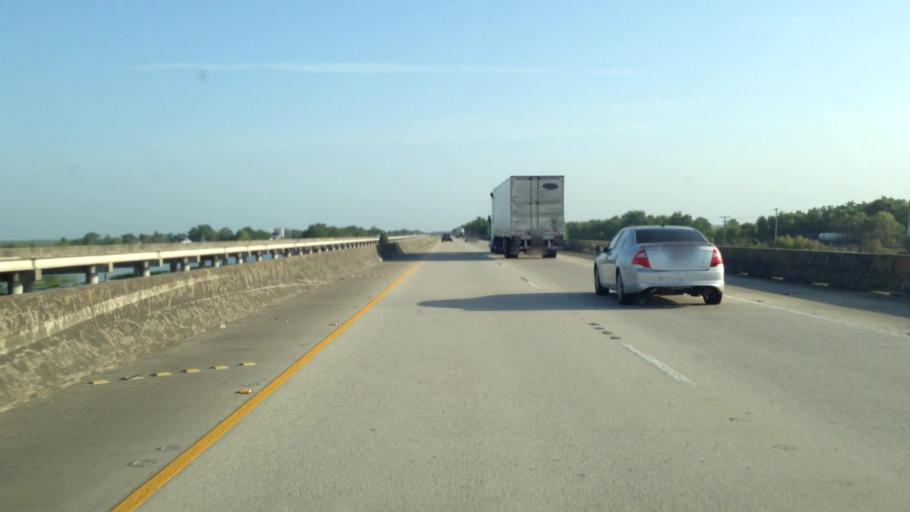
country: US
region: Louisiana
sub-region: Tangipahoa Parish
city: Ponchatoula
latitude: 30.3138
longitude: -90.4072
